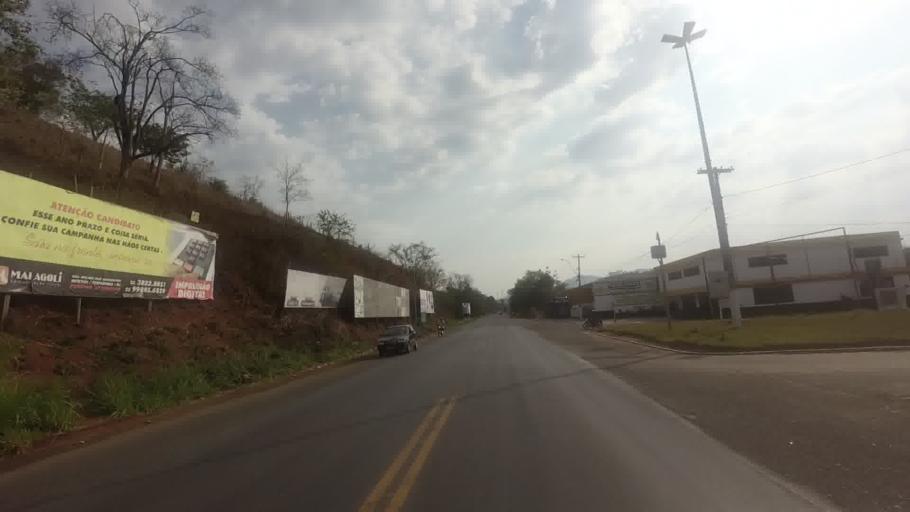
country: BR
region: Rio de Janeiro
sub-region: Itaperuna
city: Itaperuna
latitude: -21.3653
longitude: -41.9345
